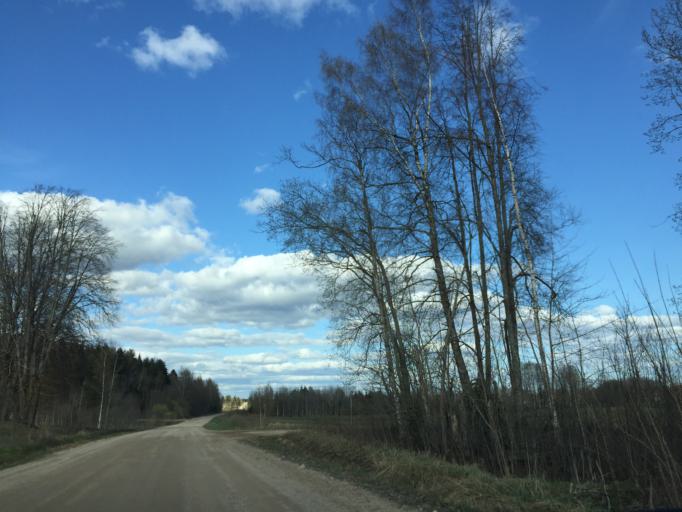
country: LV
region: Rezekne
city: Rezekne
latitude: 56.6416
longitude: 27.3238
